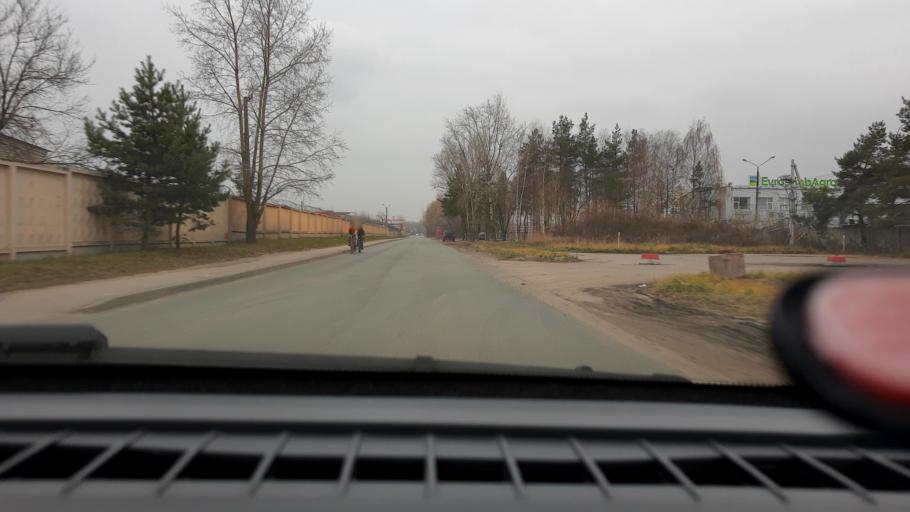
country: RU
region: Nizjnij Novgorod
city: Gorbatovka
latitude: 56.3384
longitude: 43.8066
